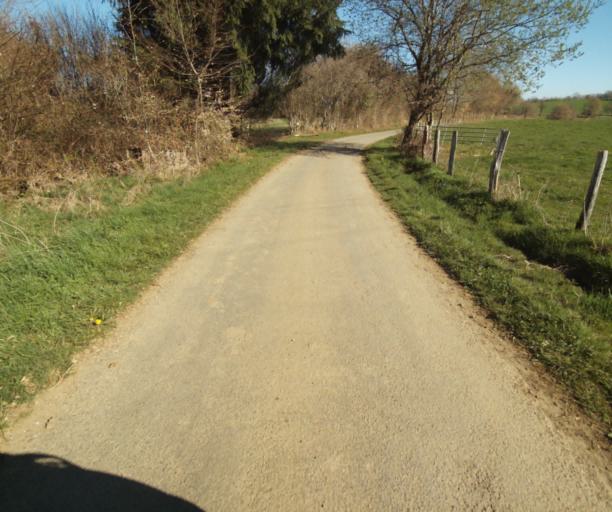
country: FR
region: Limousin
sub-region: Departement de la Correze
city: Chamboulive
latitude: 45.4002
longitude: 1.7084
